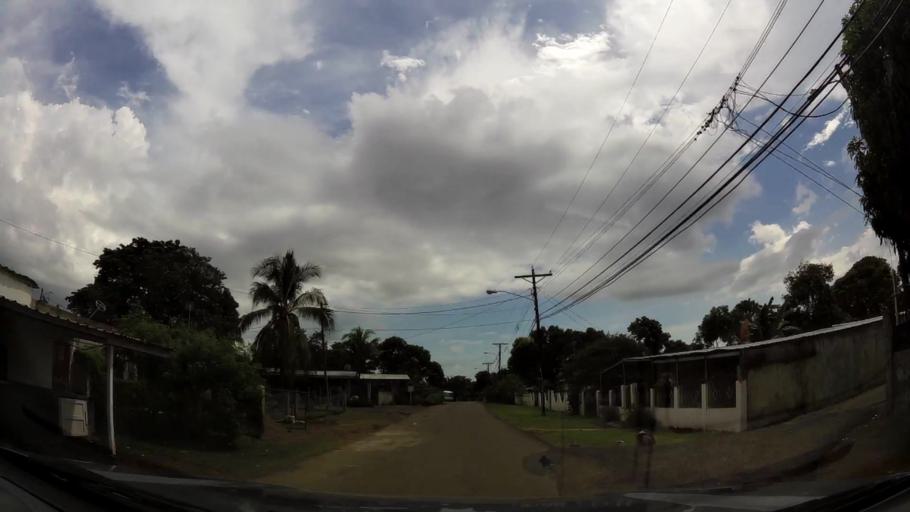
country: PA
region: Panama
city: Cabra Numero Uno
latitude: 9.1087
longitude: -79.3264
